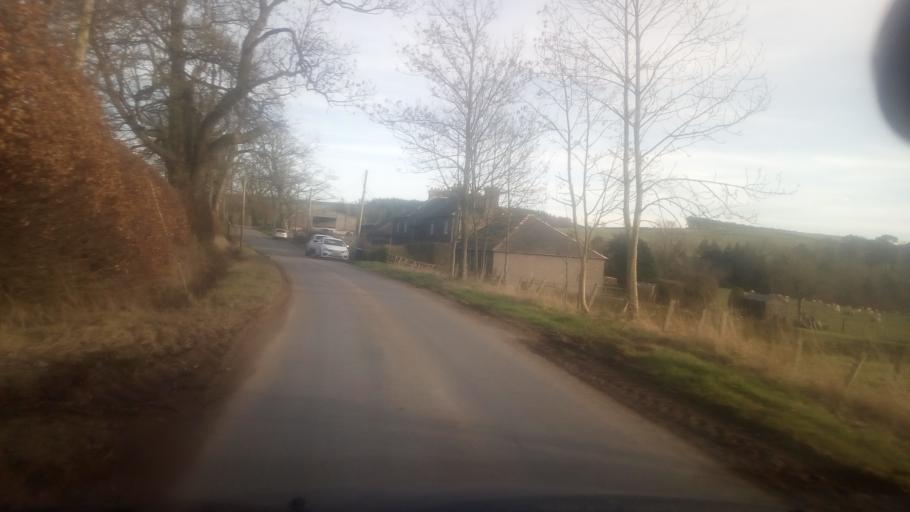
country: GB
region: Scotland
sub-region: The Scottish Borders
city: Jedburgh
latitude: 55.4095
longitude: -2.6090
